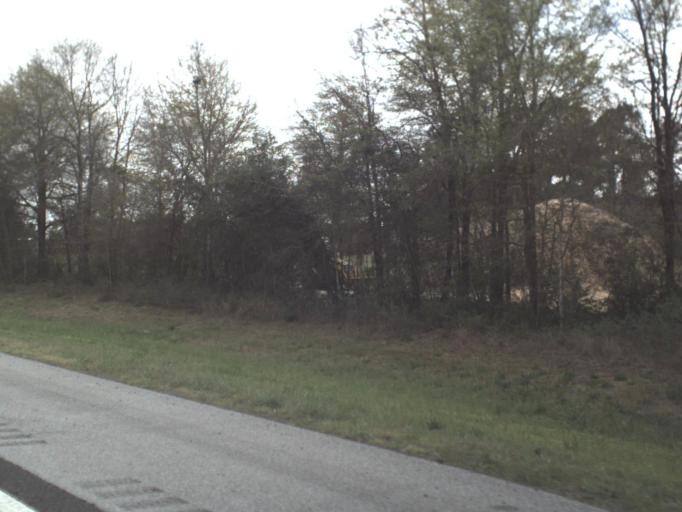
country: US
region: Florida
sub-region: Walton County
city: DeFuniak Springs
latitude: 30.7404
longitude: -86.2274
